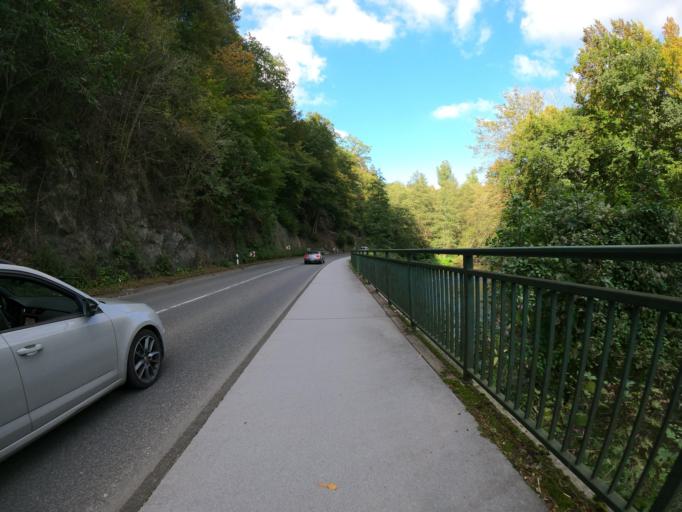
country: DE
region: North Rhine-Westphalia
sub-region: Regierungsbezirk Arnsberg
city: Schwelm
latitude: 51.2591
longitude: 7.2717
